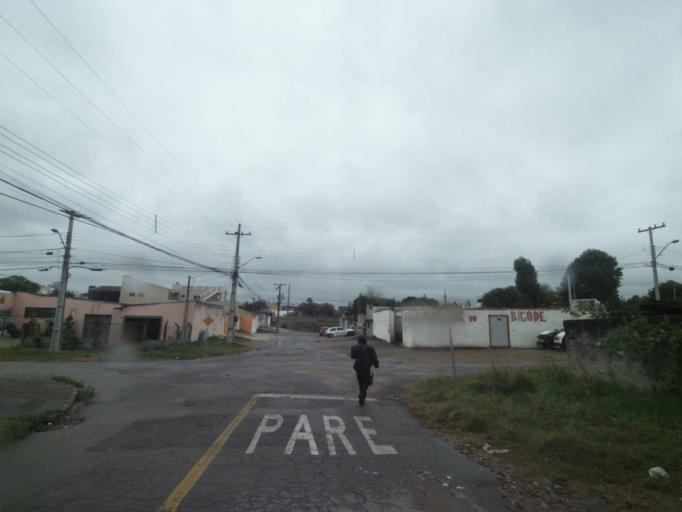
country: BR
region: Parana
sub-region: Curitiba
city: Curitiba
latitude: -25.5131
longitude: -49.3080
